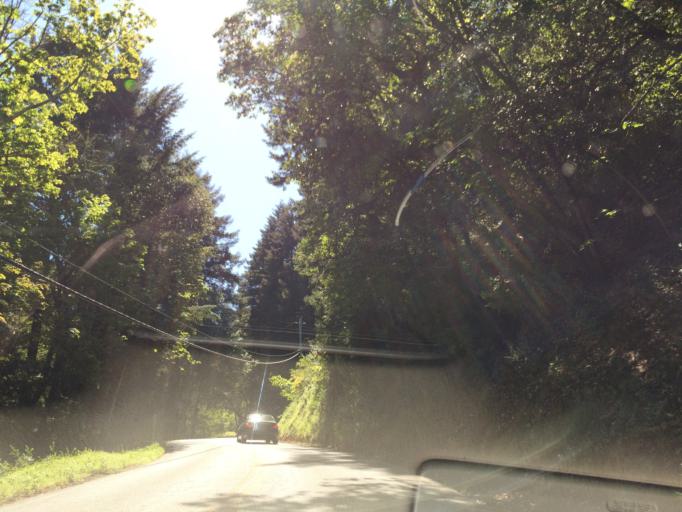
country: US
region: California
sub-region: Santa Clara County
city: Lexington Hills
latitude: 37.1698
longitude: -122.0163
